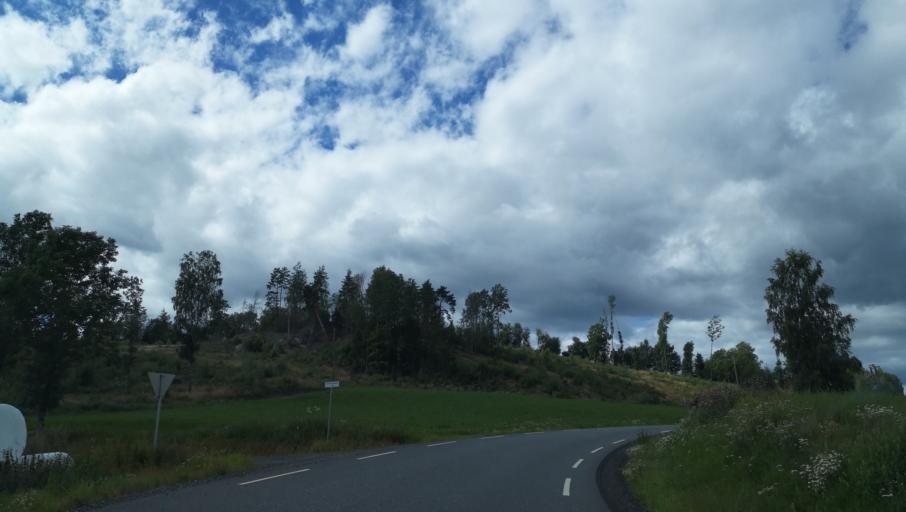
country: NO
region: Ostfold
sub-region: Hobol
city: Tomter
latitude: 59.6715
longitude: 10.9905
